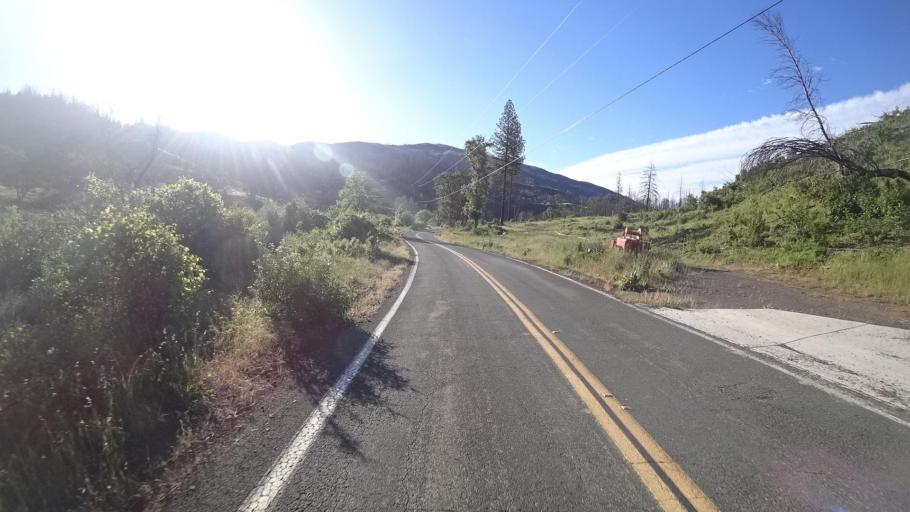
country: US
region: California
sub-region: Lake County
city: Upper Lake
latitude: 39.2459
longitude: -122.9500
